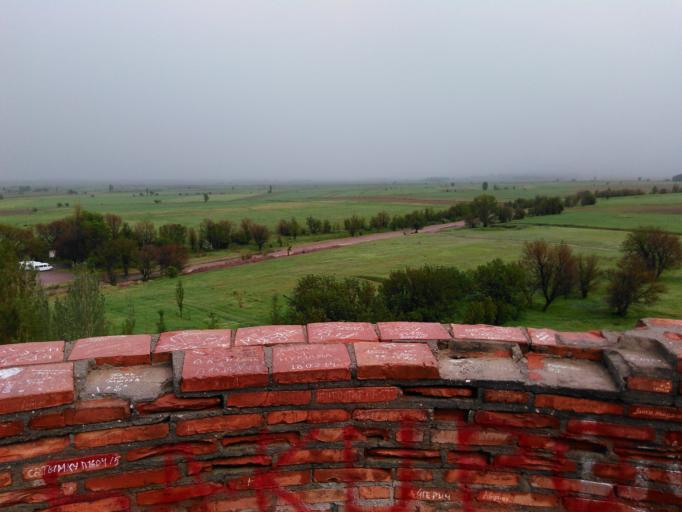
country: KG
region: Chuy
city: Chuy
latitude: 42.7464
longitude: 75.2501
